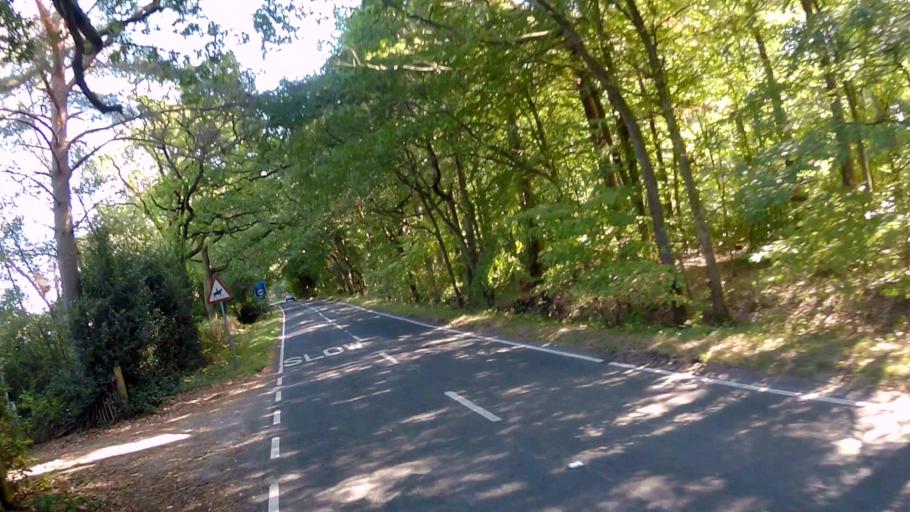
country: GB
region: England
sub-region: Surrey
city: Farnham
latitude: 51.1905
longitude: -0.7653
